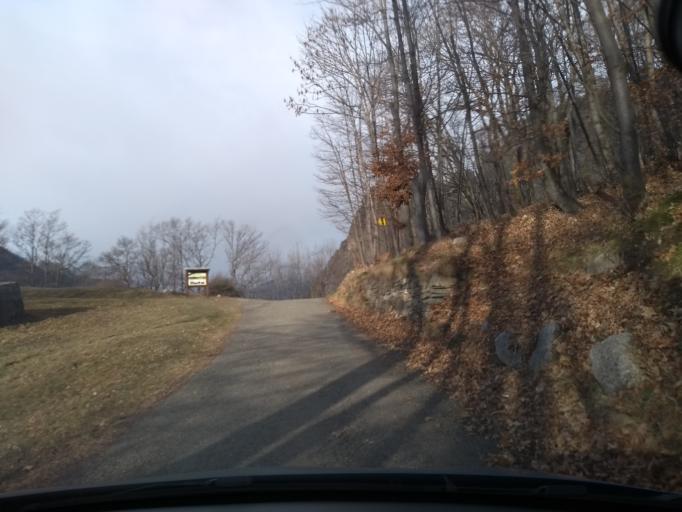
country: IT
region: Piedmont
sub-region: Provincia di Torino
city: Cantoira
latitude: 45.3503
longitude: 7.3842
